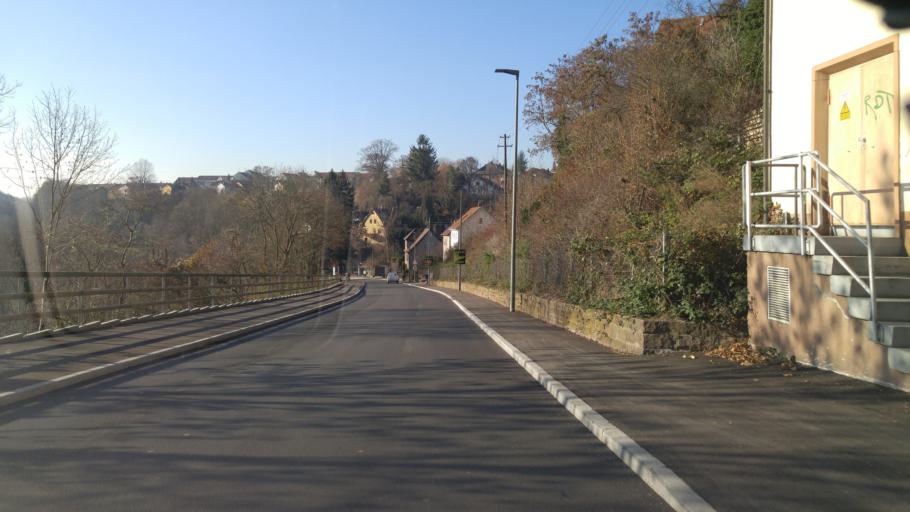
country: DE
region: Baden-Wuerttemberg
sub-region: Regierungsbezirk Stuttgart
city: Leonberg
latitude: 48.8158
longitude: 9.0152
